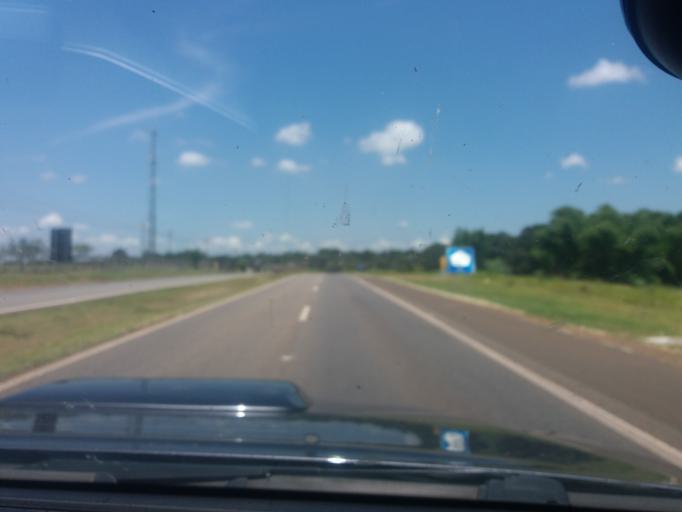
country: BR
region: Sao Paulo
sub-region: Tatui
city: Tatui
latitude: -23.3603
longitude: -47.8925
